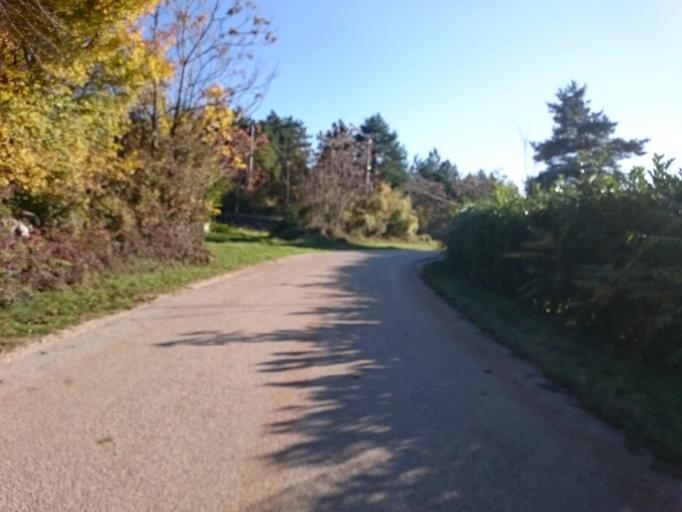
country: HR
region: Istarska
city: Buje
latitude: 45.4148
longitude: 13.7210
